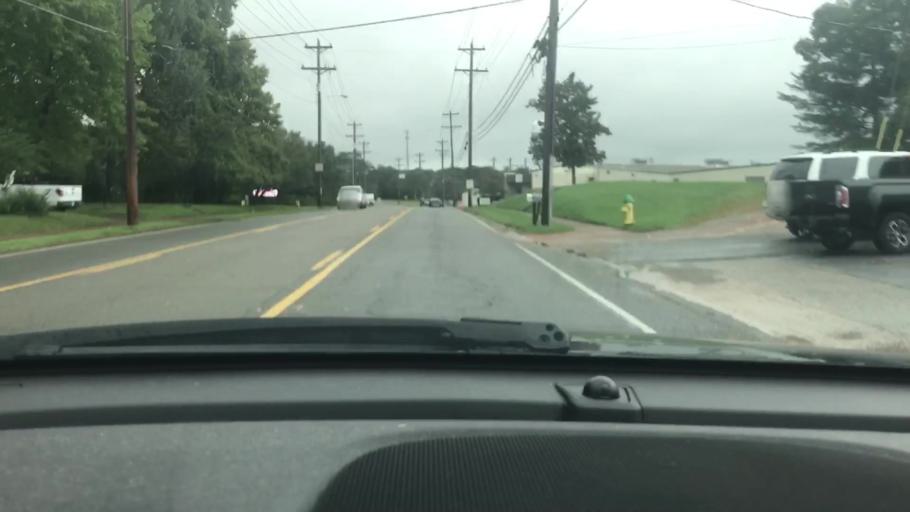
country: US
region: Tennessee
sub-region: Dickson County
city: White Bluff
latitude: 36.1062
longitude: -87.2187
